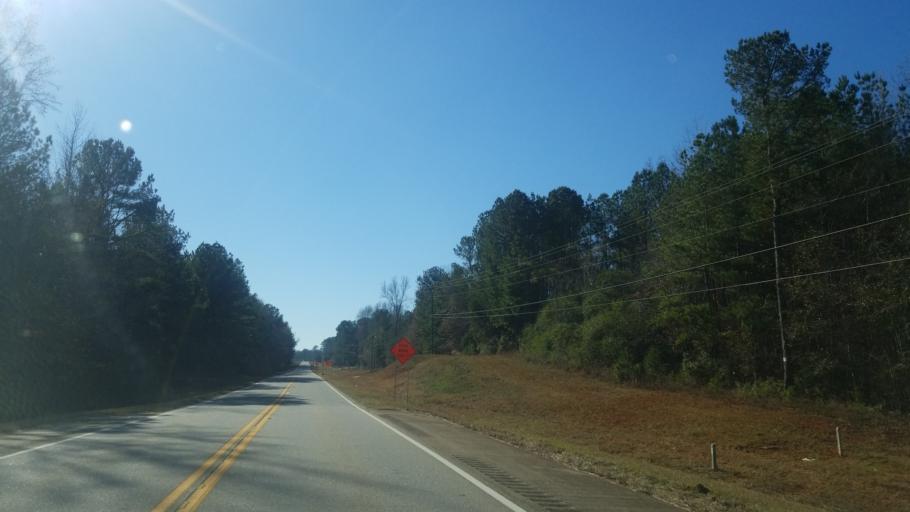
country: US
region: Alabama
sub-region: Lee County
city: Smiths Station
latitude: 32.6714
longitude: -85.0589
